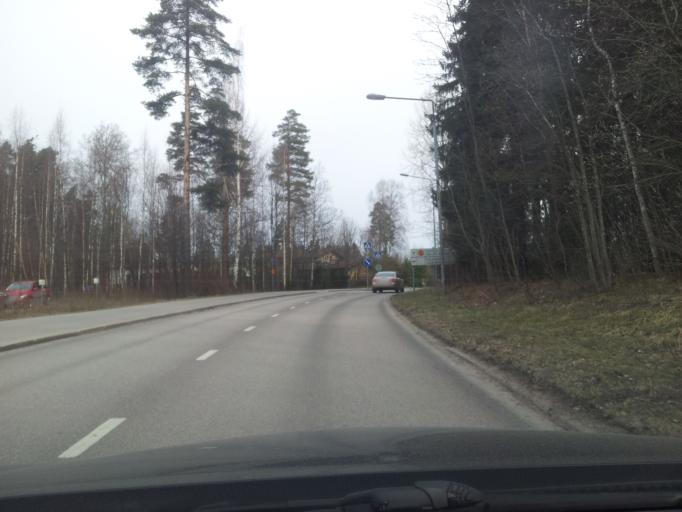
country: FI
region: Uusimaa
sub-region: Helsinki
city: Otaniemi
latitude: 60.1890
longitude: 24.7971
